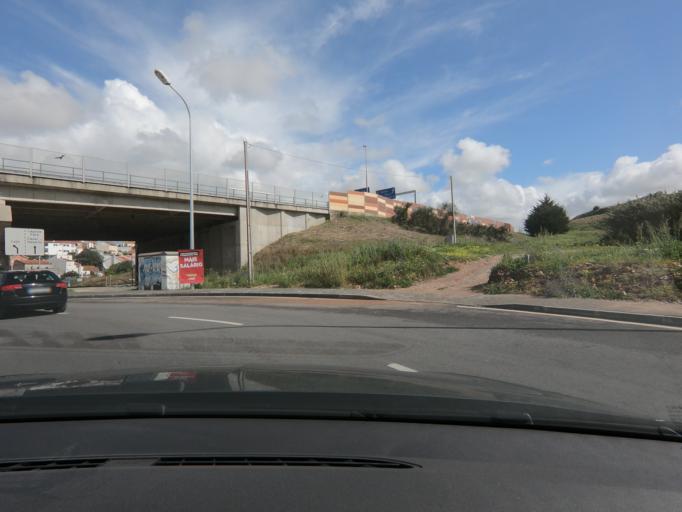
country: PT
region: Lisbon
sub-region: Cascais
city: Sao Domingos de Rana
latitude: 38.7088
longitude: -9.3127
